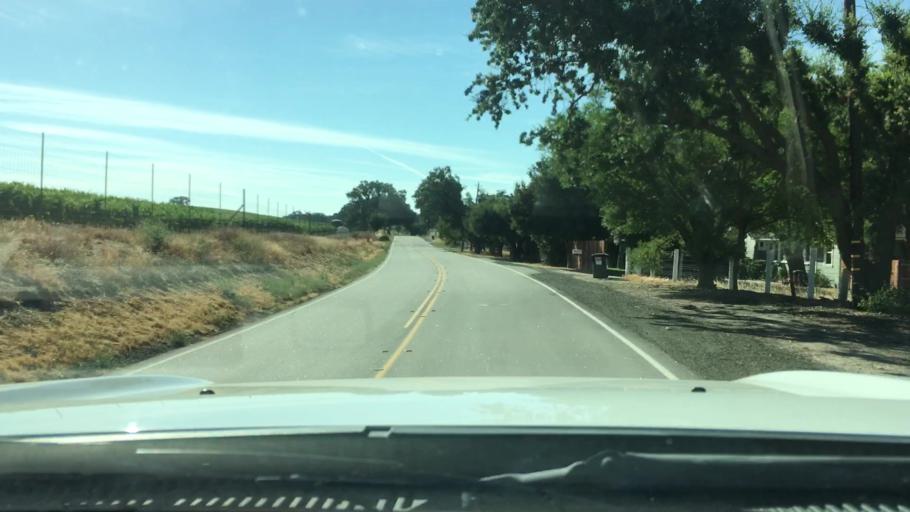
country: US
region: California
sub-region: San Luis Obispo County
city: Templeton
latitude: 35.5563
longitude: -120.6265
